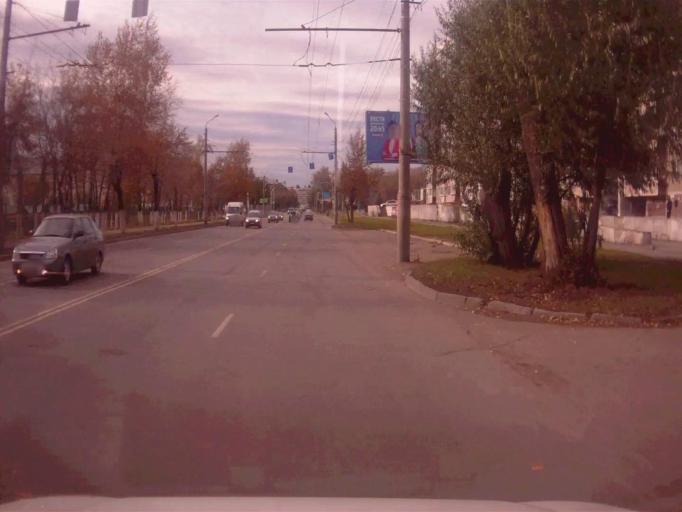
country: RU
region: Chelyabinsk
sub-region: Gorod Chelyabinsk
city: Chelyabinsk
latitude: 55.1139
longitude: 61.4568
